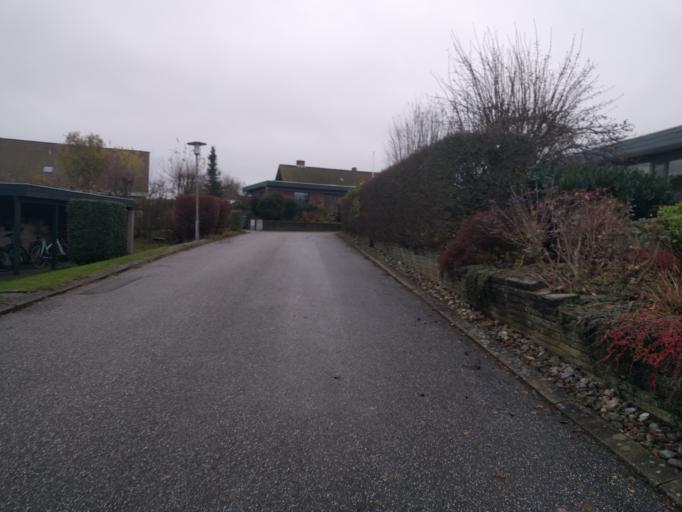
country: DK
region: South Denmark
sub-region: Fredericia Kommune
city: Snoghoj
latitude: 55.5417
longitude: 9.7286
